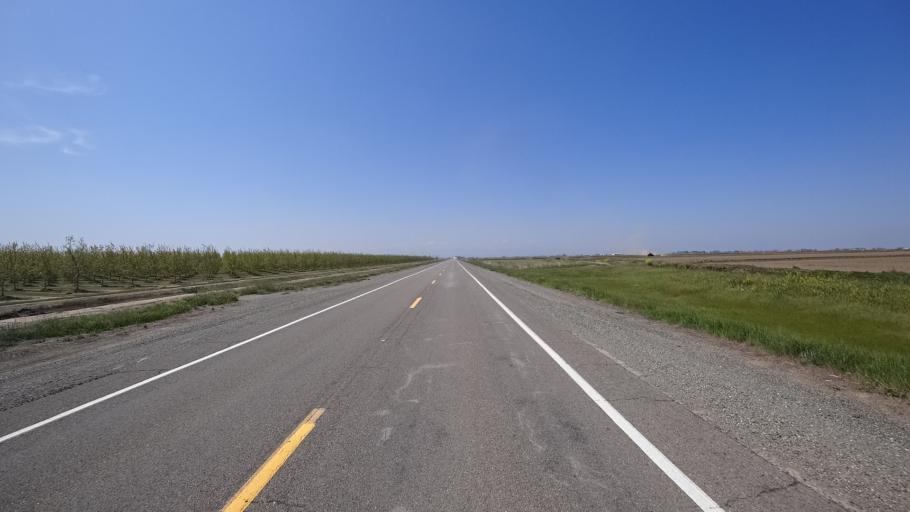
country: US
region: California
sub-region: Glenn County
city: Willows
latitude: 39.5219
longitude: -122.0513
